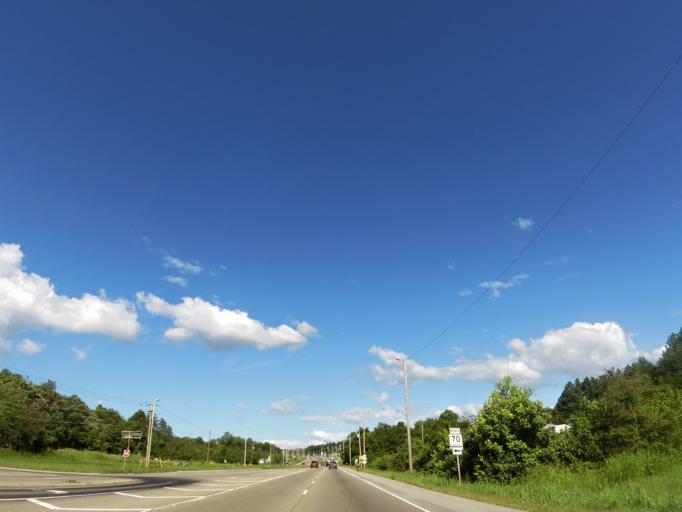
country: US
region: Tennessee
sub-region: Greene County
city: Greeneville
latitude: 36.1725
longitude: -82.8508
